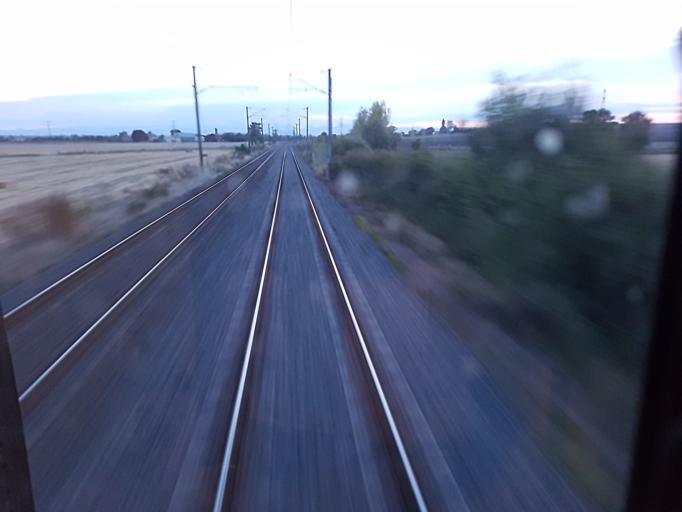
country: FR
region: Auvergne
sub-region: Departement du Puy-de-Dome
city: Maringues
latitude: 45.9806
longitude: 3.2893
